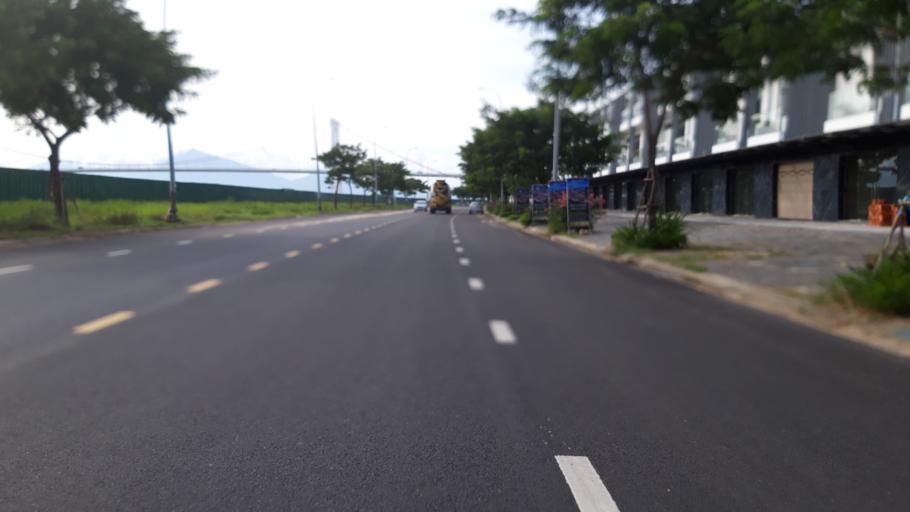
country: VN
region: Da Nang
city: Da Nang
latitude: 16.0911
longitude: 108.2265
